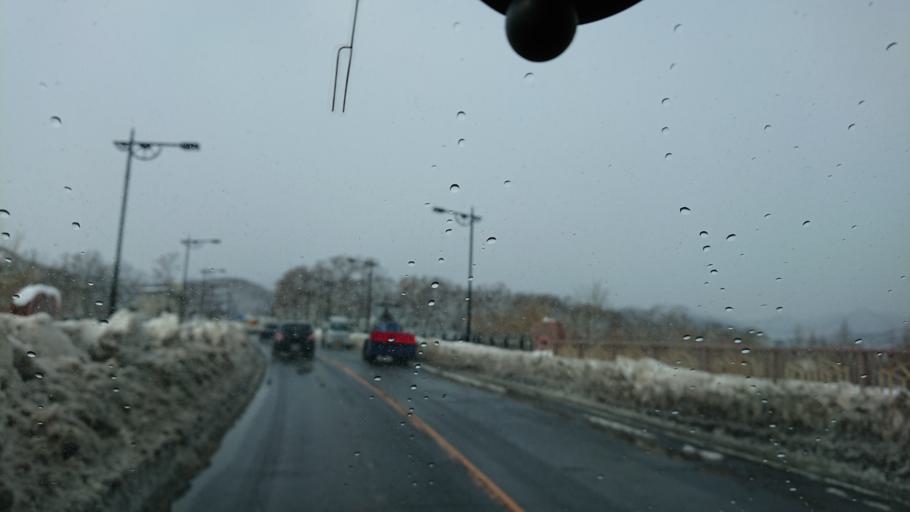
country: JP
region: Hokkaido
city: Sapporo
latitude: 42.9829
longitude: 141.3415
